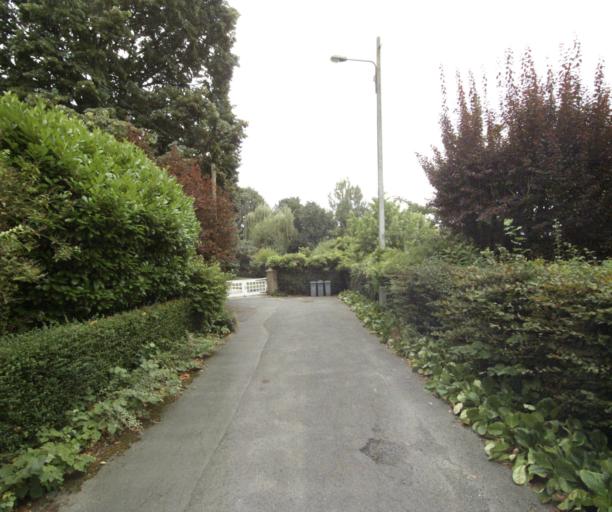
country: FR
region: Nord-Pas-de-Calais
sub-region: Departement du Nord
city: Croix
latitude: 50.6694
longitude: 3.1641
